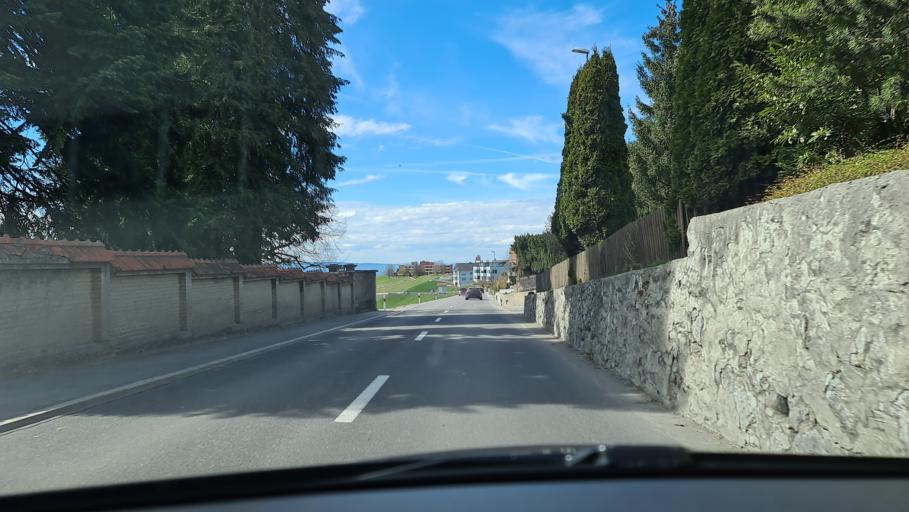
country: CH
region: Zug
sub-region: Zug
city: Menzingen
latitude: 47.1785
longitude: 8.5871
